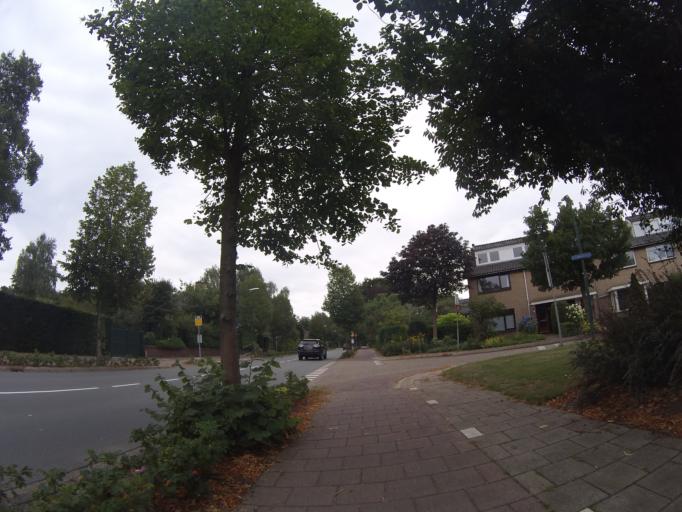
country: NL
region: Utrecht
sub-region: Gemeente Baarn
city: Baarn
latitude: 52.2199
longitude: 5.2625
